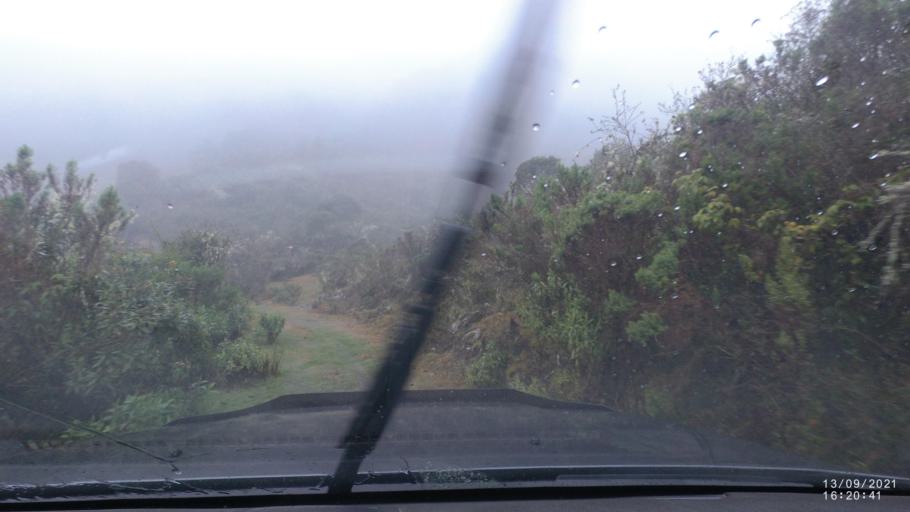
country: BO
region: Cochabamba
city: Colomi
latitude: -17.2686
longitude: -65.7035
